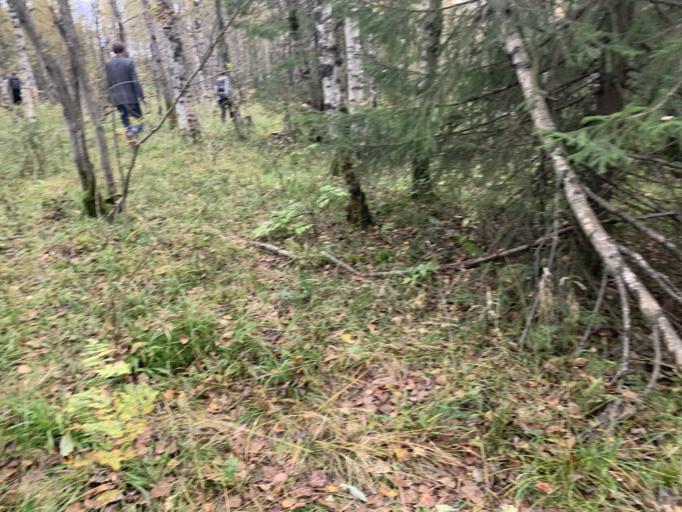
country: RU
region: Perm
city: Gubakha
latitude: 58.8464
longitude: 57.5801
